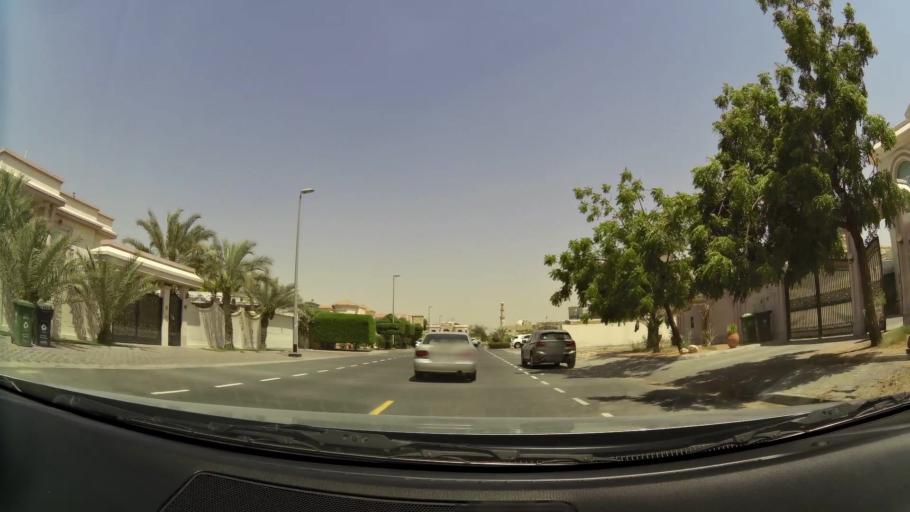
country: AE
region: Dubai
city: Dubai
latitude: 25.1076
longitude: 55.2209
